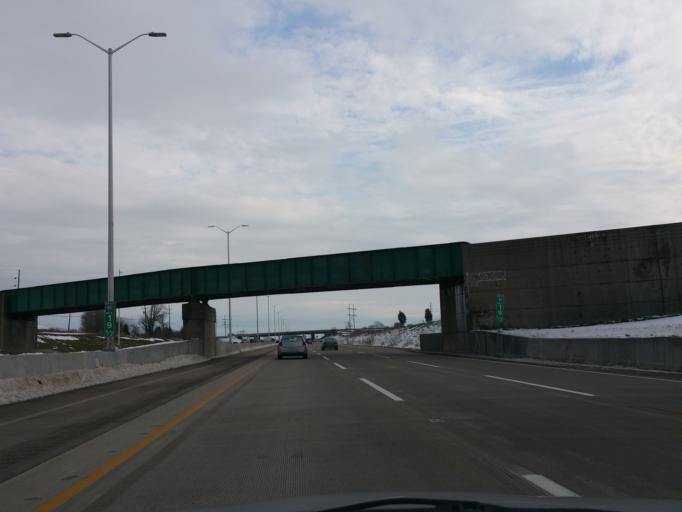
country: US
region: Illinois
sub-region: Winnebago County
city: Cherry Valley
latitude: 42.2427
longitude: -88.9223
